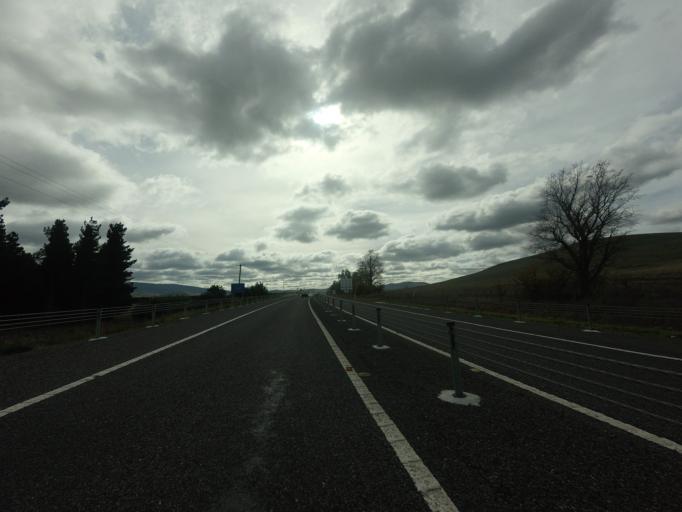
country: AU
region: Tasmania
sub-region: Brighton
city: Bridgewater
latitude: -42.5164
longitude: 147.1902
